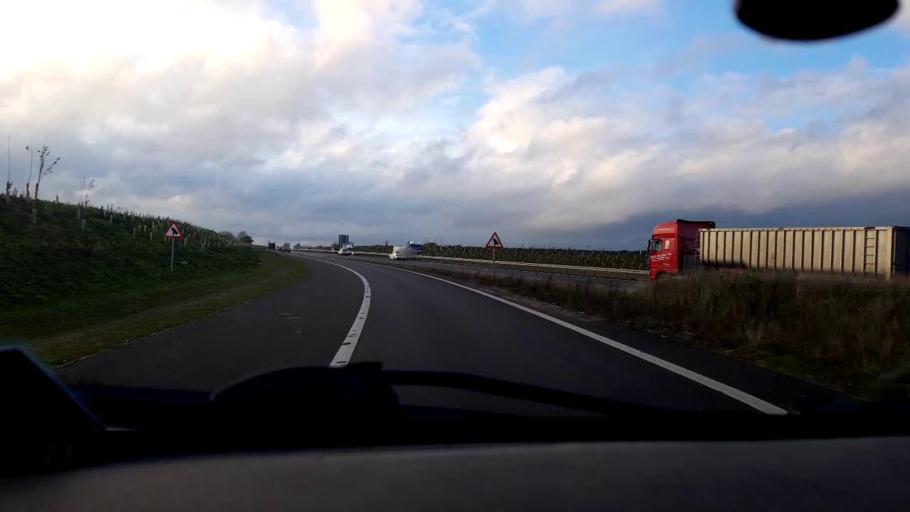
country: GB
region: England
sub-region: Norfolk
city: Horsford
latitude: 52.6813
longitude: 1.2581
